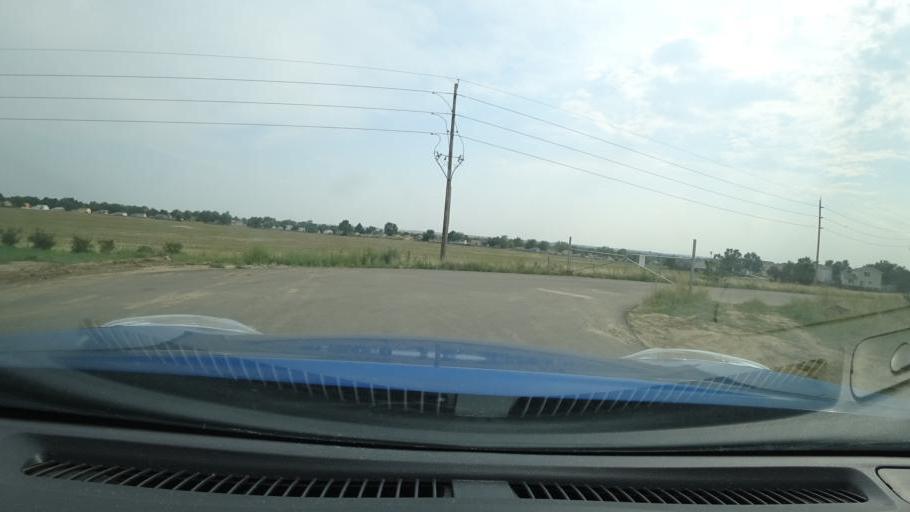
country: US
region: Colorado
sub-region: Adams County
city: Aurora
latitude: 39.7475
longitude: -104.7535
